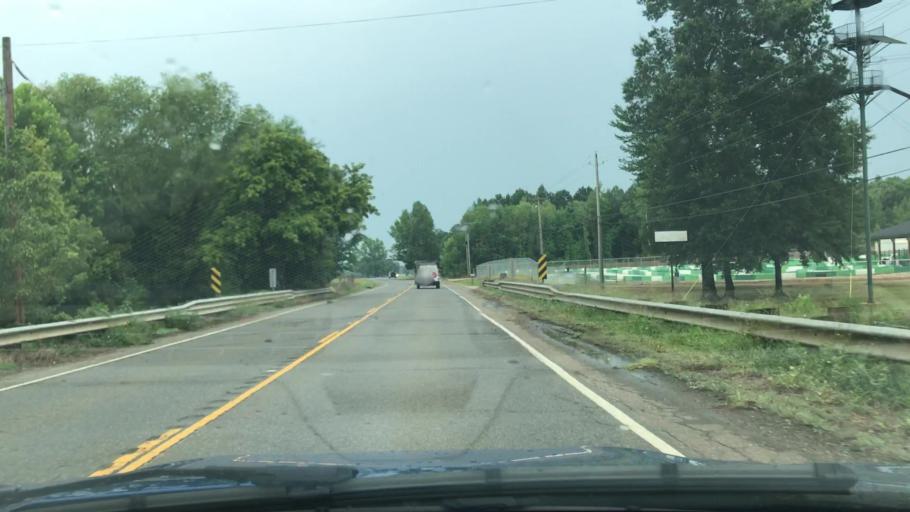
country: US
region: Texas
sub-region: Harrison County
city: Waskom
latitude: 32.4668
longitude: -94.0371
